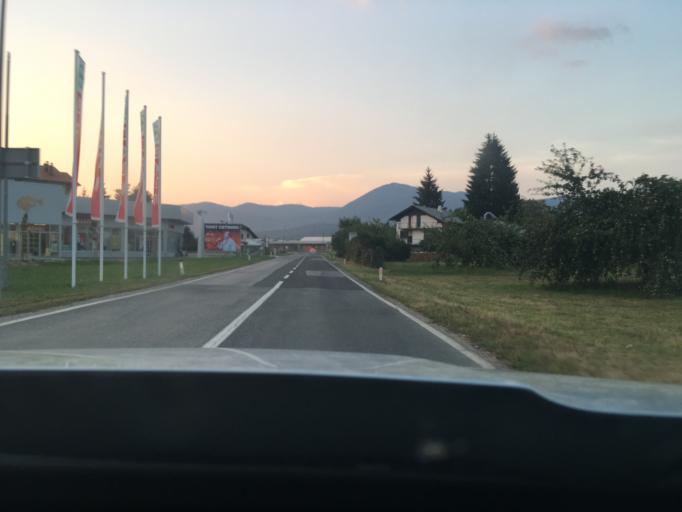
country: SI
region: Ribnica
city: Ribnica
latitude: 45.7361
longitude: 14.7337
